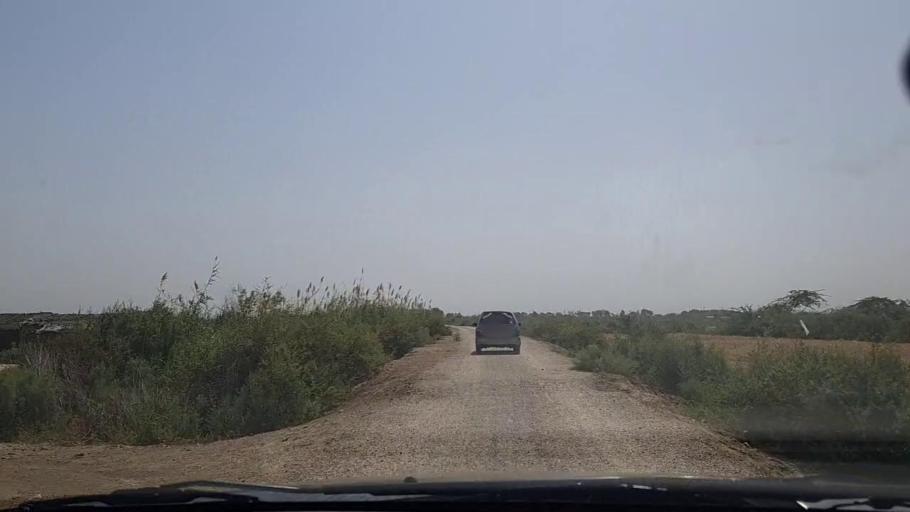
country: PK
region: Sindh
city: Mirpur Sakro
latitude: 24.3248
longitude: 67.6840
